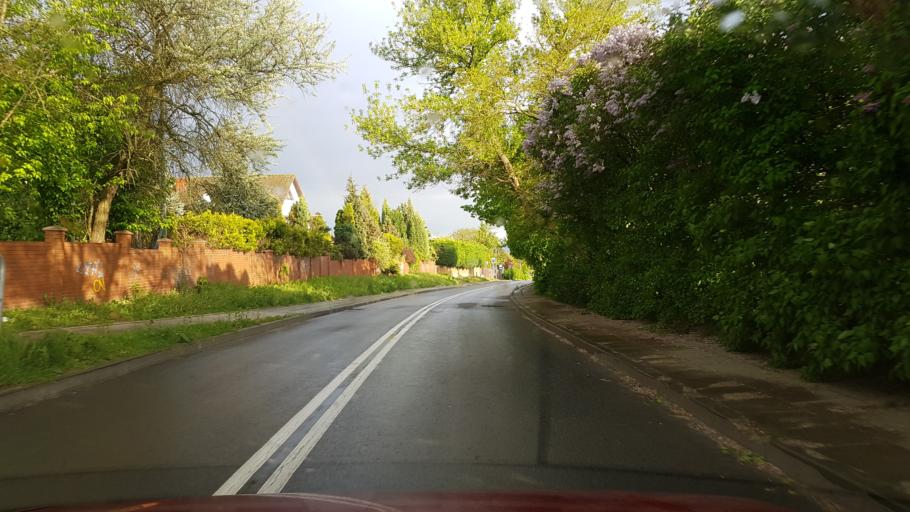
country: PL
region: West Pomeranian Voivodeship
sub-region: Szczecin
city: Szczecin
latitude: 53.4675
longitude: 14.5516
